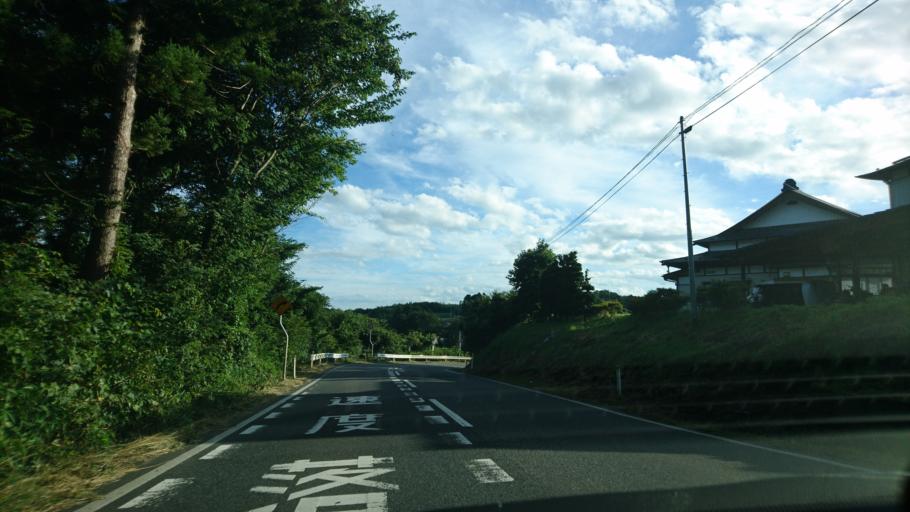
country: JP
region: Iwate
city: Ichinoseki
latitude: 38.8809
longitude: 141.2171
